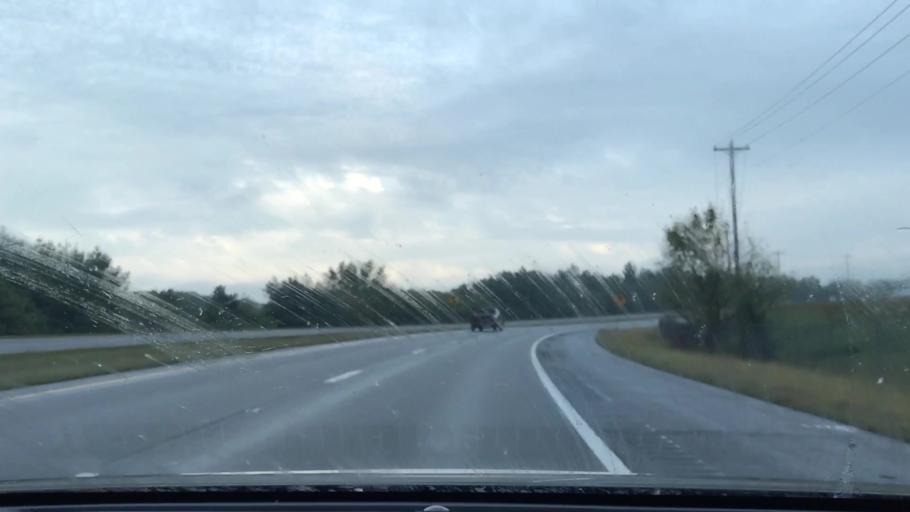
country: US
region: Tennessee
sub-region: Sumner County
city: Gallatin
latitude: 36.3942
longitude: -86.4795
